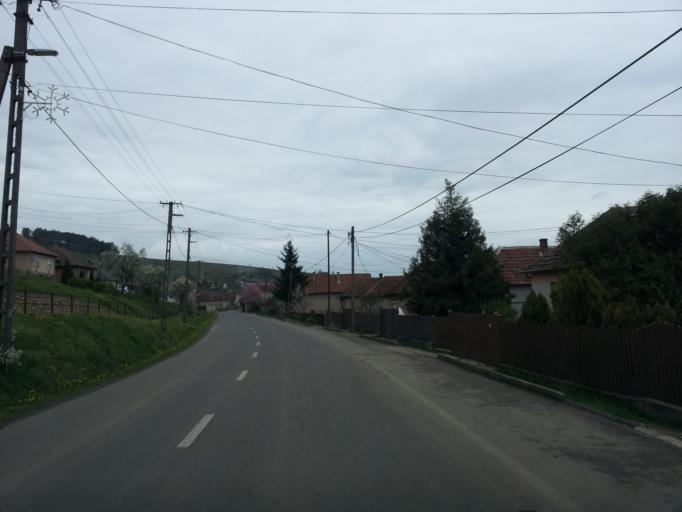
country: HU
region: Borsod-Abauj-Zemplen
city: Rudabanya
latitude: 48.4949
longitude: 20.6541
